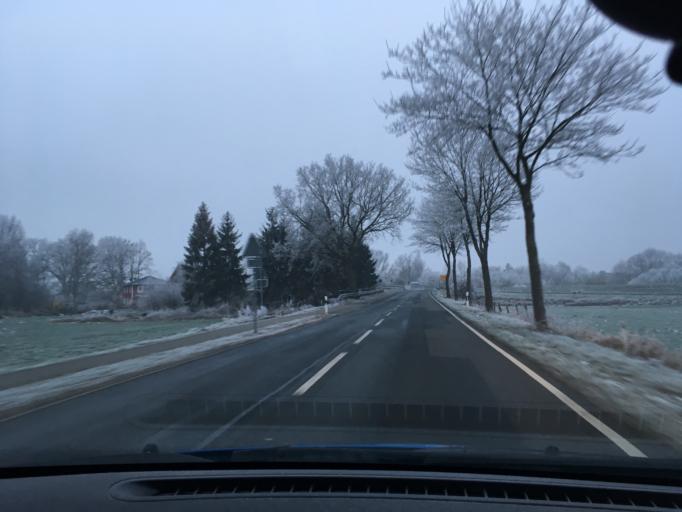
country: DE
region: Lower Saxony
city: Stelle
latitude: 53.3889
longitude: 10.1157
